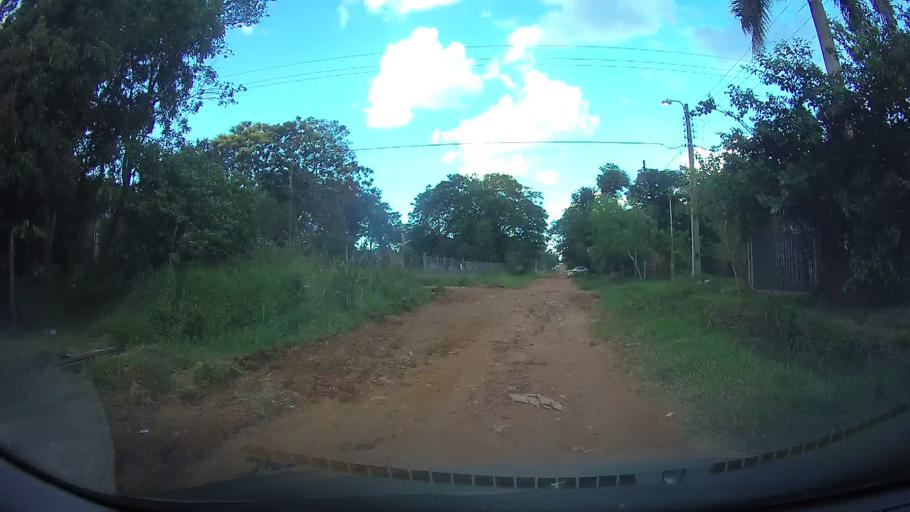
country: PY
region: Central
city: Limpio
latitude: -25.2510
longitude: -57.4585
